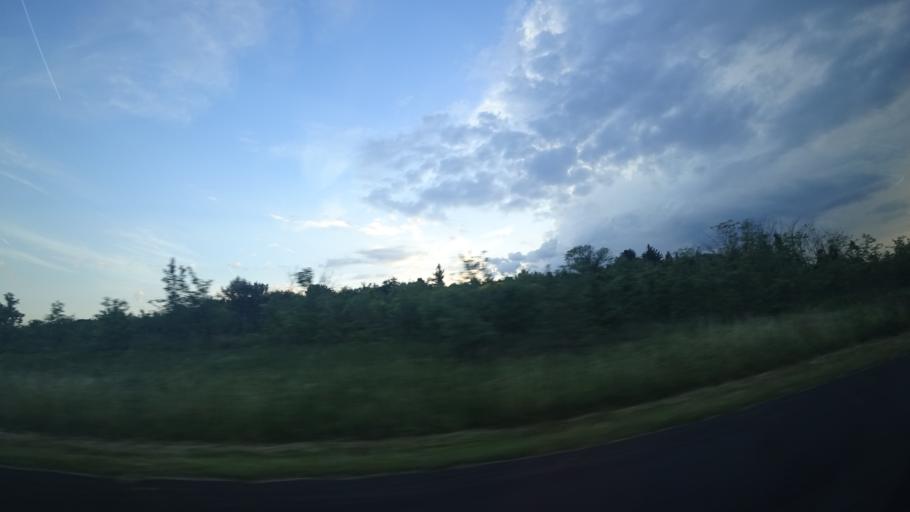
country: FR
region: Languedoc-Roussillon
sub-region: Departement de l'Herault
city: Nebian
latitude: 43.5985
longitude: 3.4628
